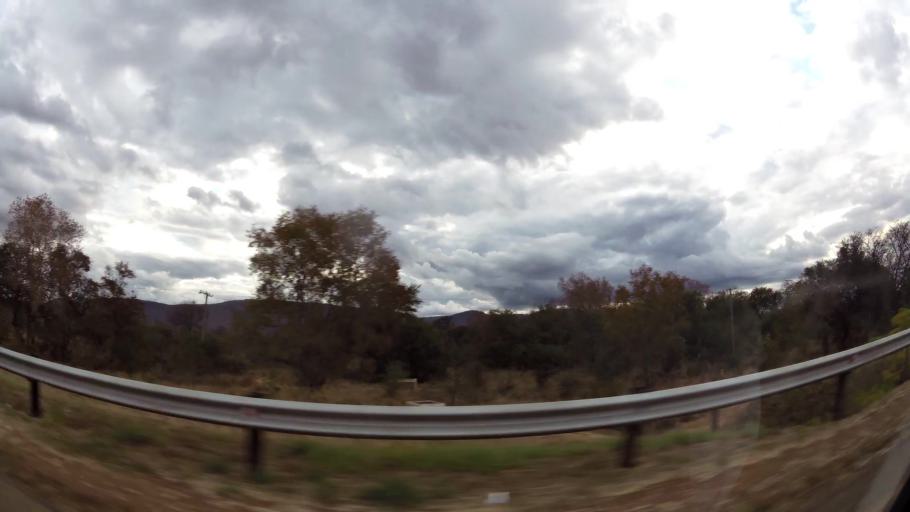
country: ZA
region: Limpopo
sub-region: Waterberg District Municipality
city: Mokopane
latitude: -24.2162
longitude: 29.0055
